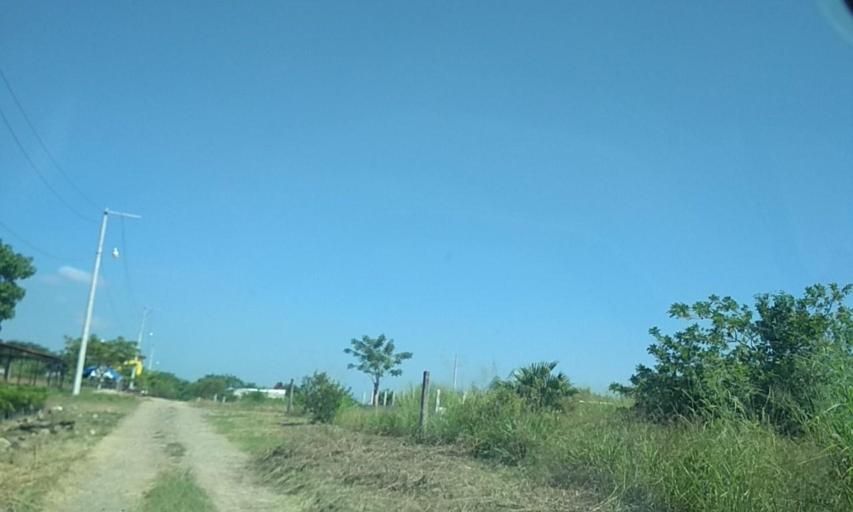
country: MX
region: Veracruz
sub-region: Martinez de la Torre
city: La Union Paso Largo
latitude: 20.1497
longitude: -97.0005
